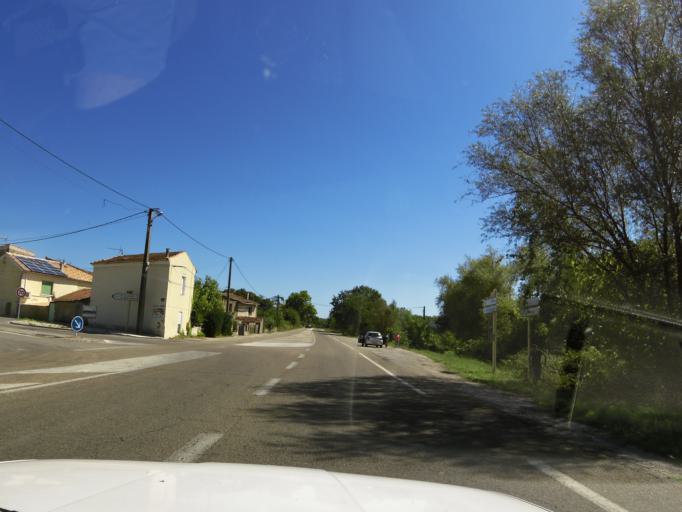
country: FR
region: Languedoc-Roussillon
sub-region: Departement du Gard
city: Saint-Hilaire-de-Brethmas
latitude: 44.0838
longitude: 4.1119
